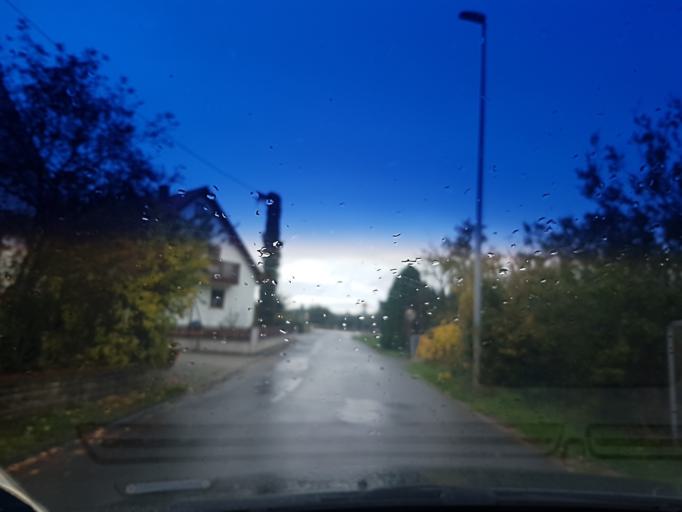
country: DE
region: Bavaria
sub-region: Regierungsbezirk Mittelfranken
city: Burghaslach
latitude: 49.7642
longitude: 10.5696
